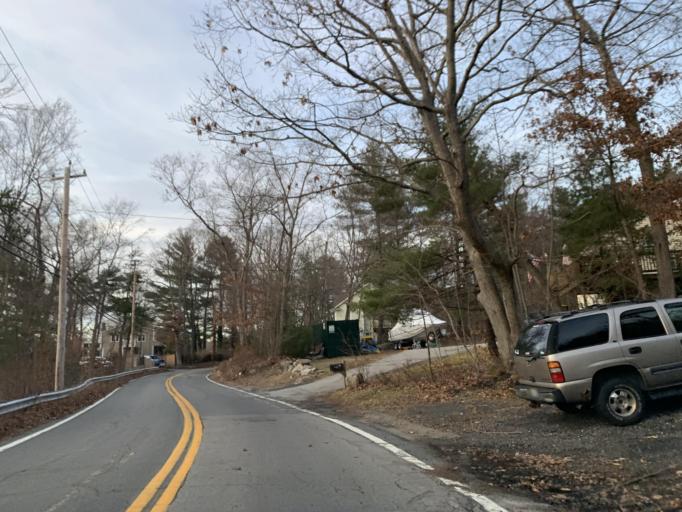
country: US
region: Rhode Island
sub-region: Providence County
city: Pascoag
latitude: 41.9486
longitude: -71.7023
